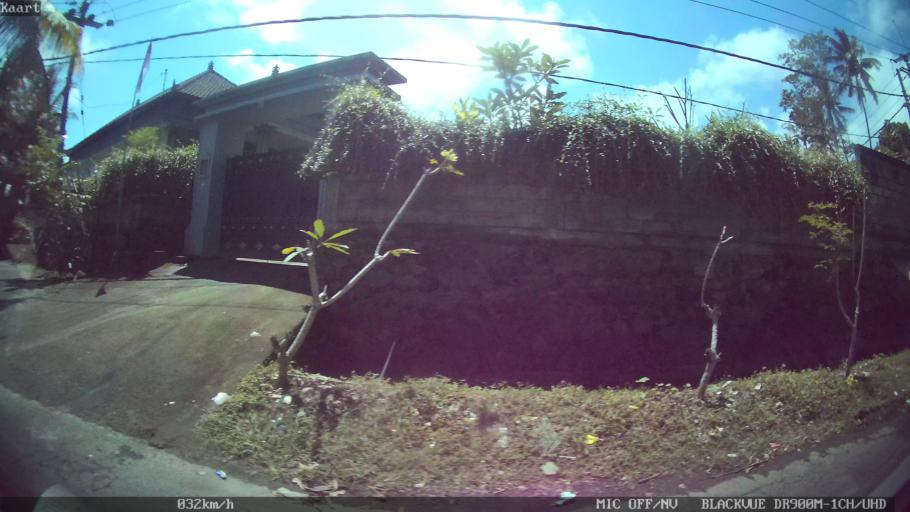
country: ID
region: Bali
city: Banjar Kelodan
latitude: -8.5122
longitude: 115.3351
